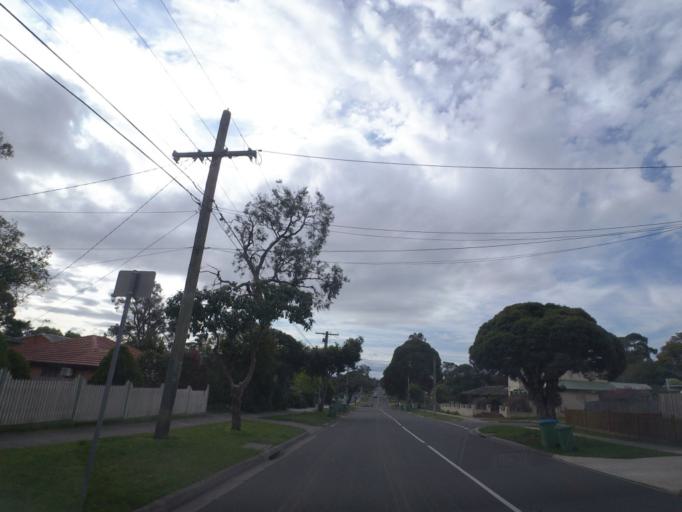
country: AU
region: Victoria
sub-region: Maroondah
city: Heathmont
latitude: -37.8273
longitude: 145.2373
